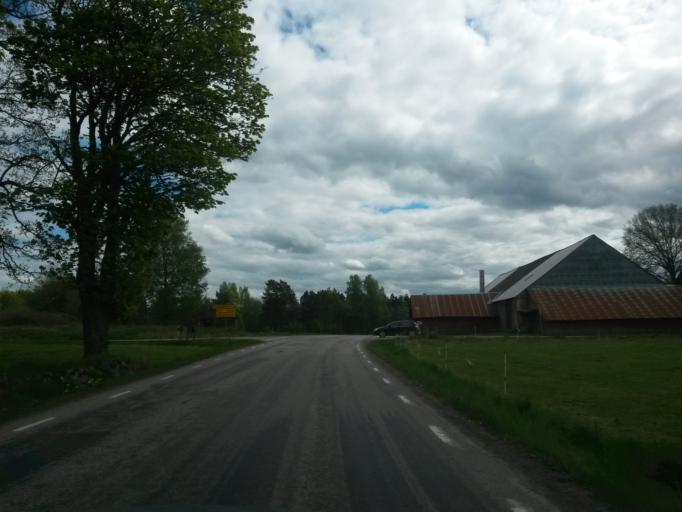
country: SE
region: Vaestra Goetaland
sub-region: Essunga Kommun
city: Nossebro
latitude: 58.1377
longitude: 12.7741
